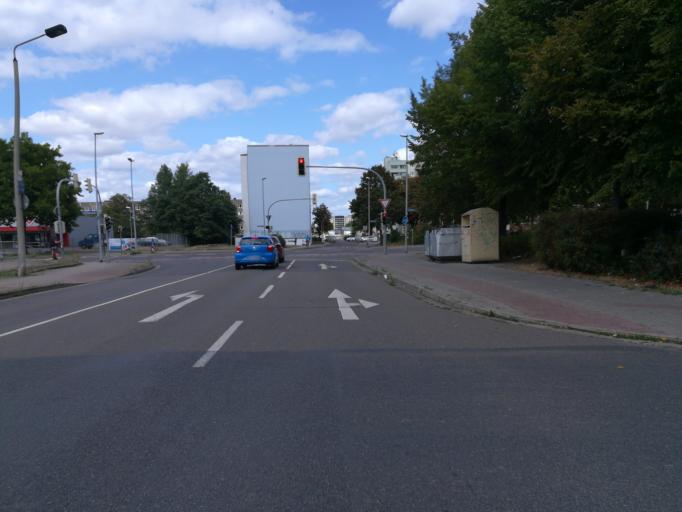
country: DE
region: Saxony-Anhalt
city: Neue Neustadt
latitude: 52.1599
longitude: 11.6311
